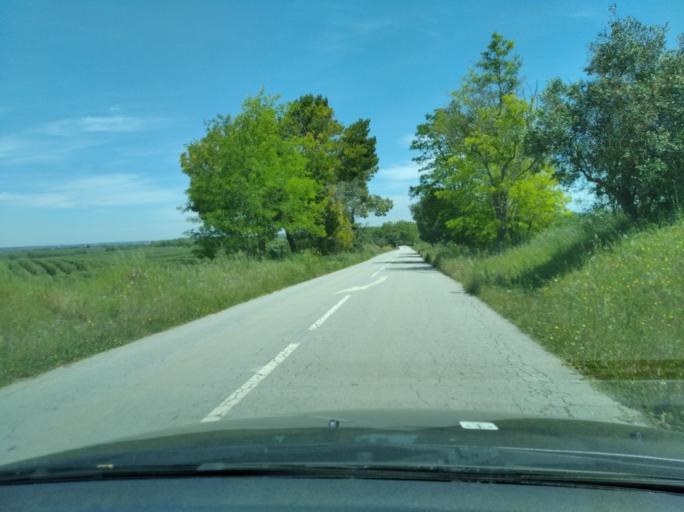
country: PT
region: Portalegre
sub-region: Avis
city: Avis
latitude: 39.0702
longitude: -7.8846
